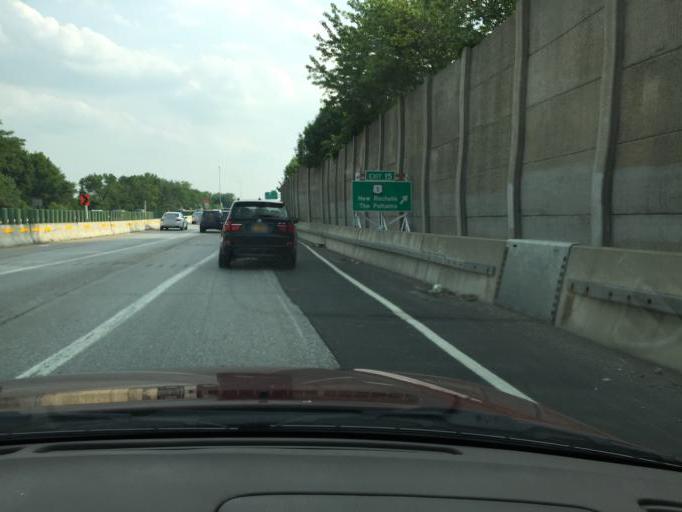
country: US
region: New York
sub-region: Westchester County
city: New Rochelle
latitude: 40.9043
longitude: -73.7927
